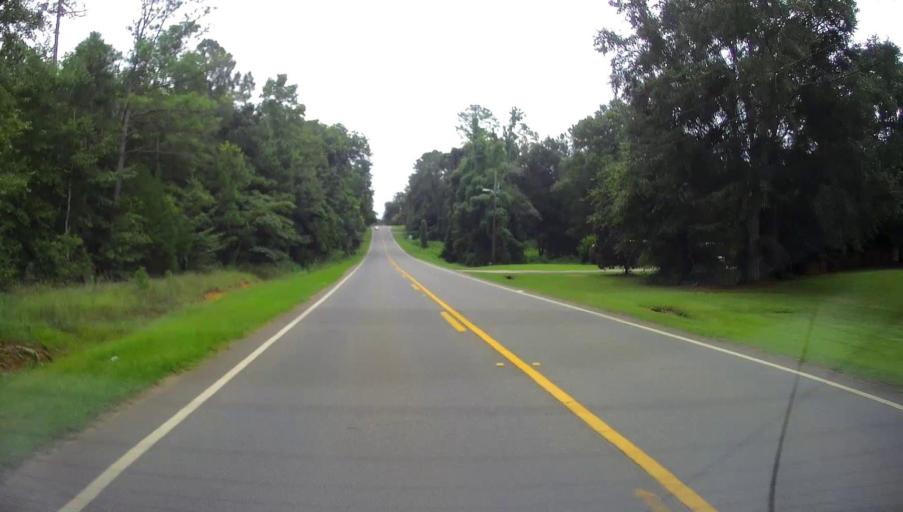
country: US
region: Georgia
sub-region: Schley County
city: Ellaville
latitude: 32.2431
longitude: -84.3190
